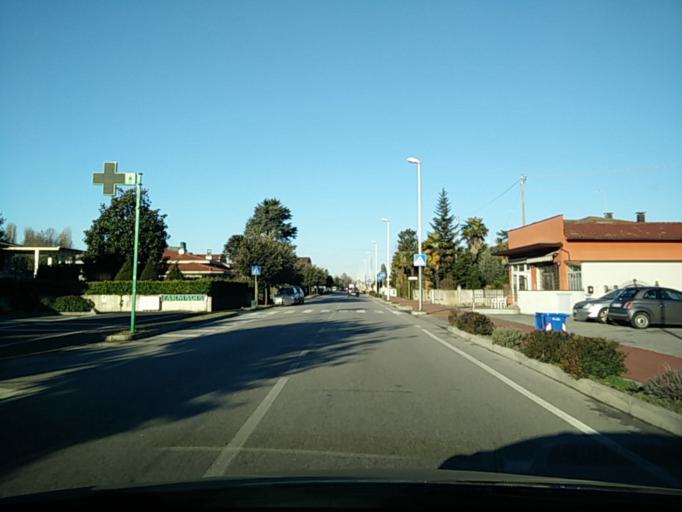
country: IT
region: Veneto
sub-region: Provincia di Venezia
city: Pianiga
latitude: 45.4567
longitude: 12.0273
